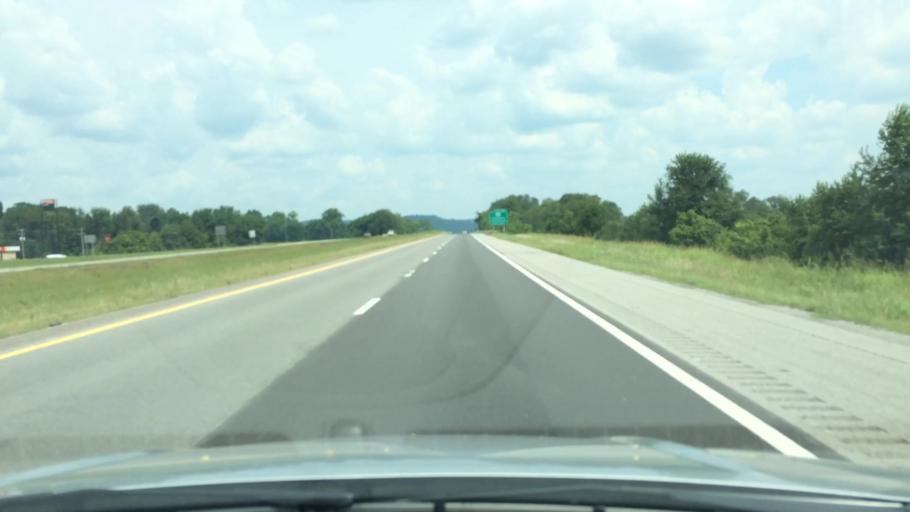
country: US
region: Tennessee
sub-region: Marshall County
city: Cornersville
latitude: 35.3028
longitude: -86.8823
